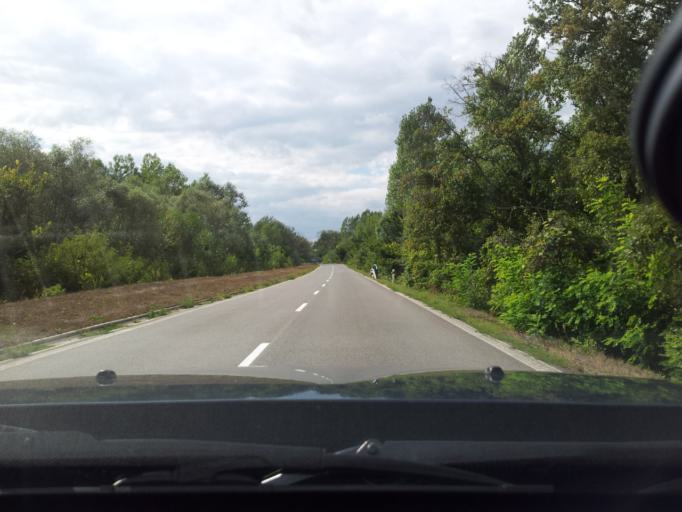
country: SK
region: Kosicky
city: Michalovce
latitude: 48.5704
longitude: 21.9592
